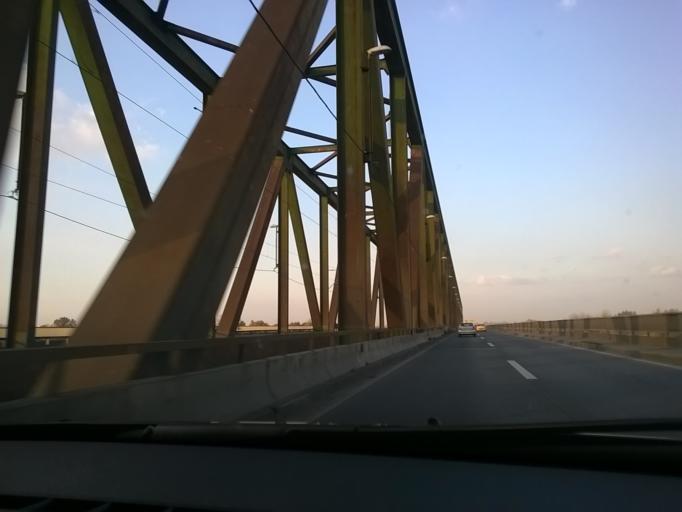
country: RS
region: Central Serbia
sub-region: Belgrade
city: Palilula
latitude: 44.8279
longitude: 20.4919
